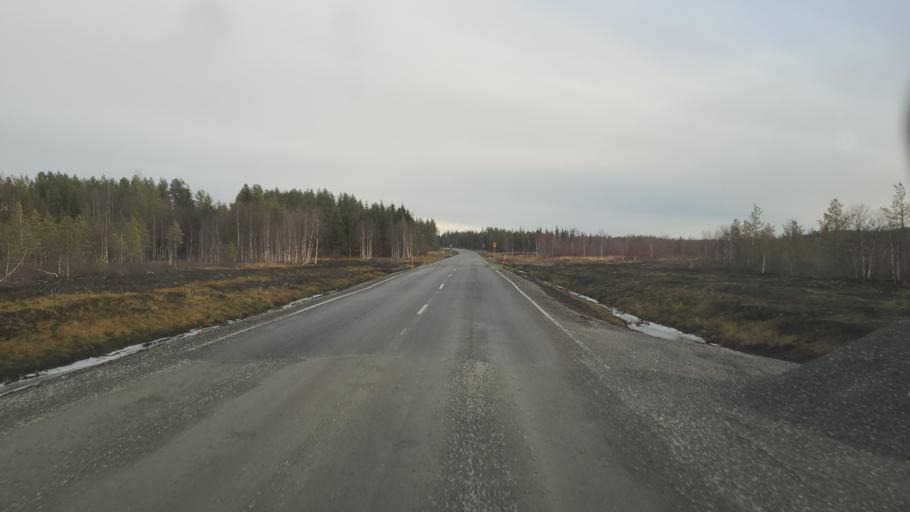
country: FI
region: Lapland
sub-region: Tunturi-Lappi
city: Kittilae
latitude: 67.8646
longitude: 24.9622
